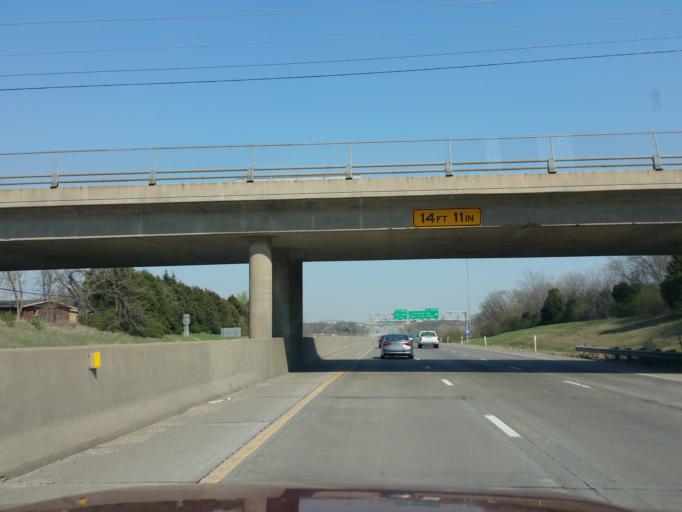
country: US
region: Kansas
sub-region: Shawnee County
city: Topeka
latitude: 39.0344
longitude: -95.6445
